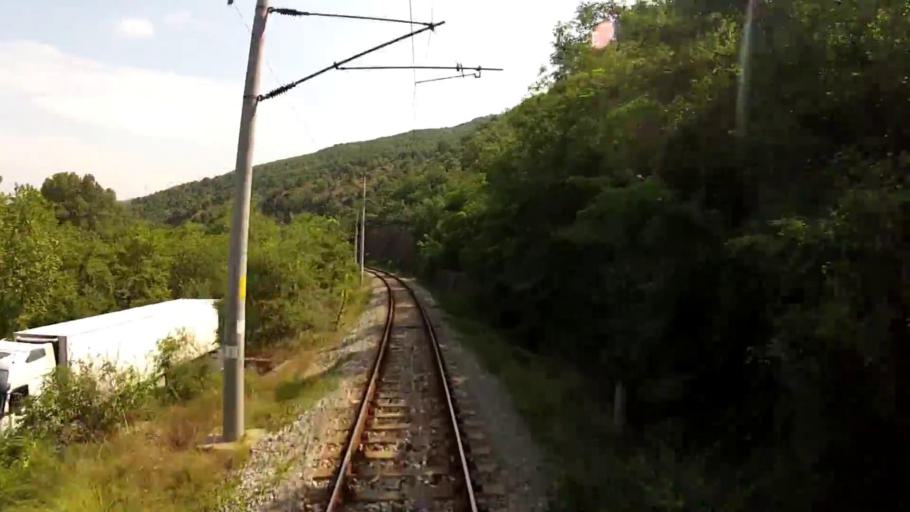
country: BG
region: Blagoevgrad
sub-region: Obshtina Kresna
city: Kresna
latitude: 41.7149
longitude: 23.1715
